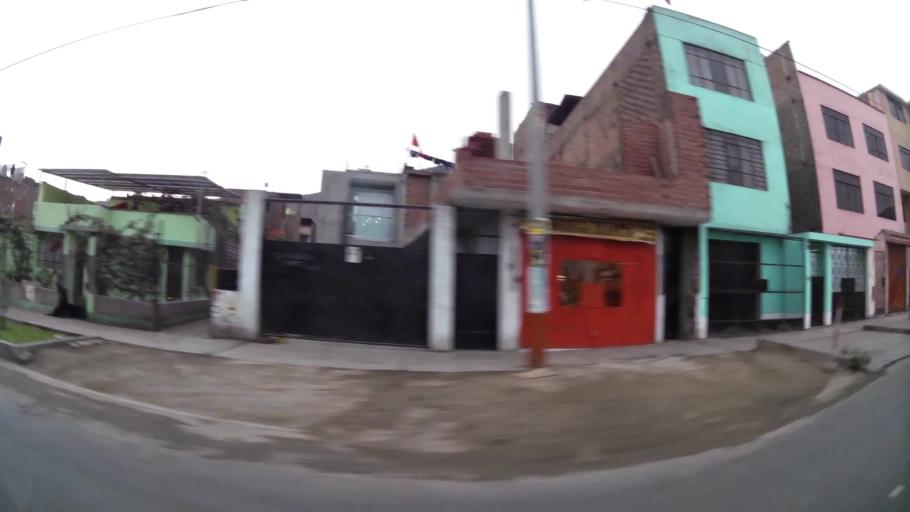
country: PE
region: Lima
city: Lima
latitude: -12.0117
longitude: -76.9837
